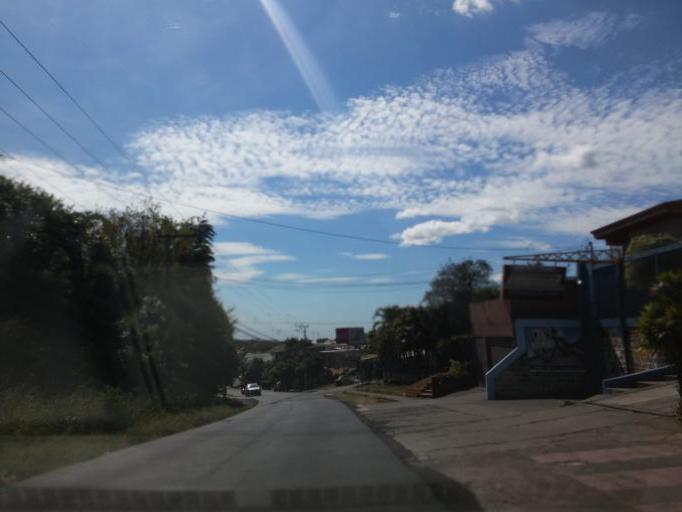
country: CR
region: Heredia
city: Santo Domingo
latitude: 10.0352
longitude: -84.1628
